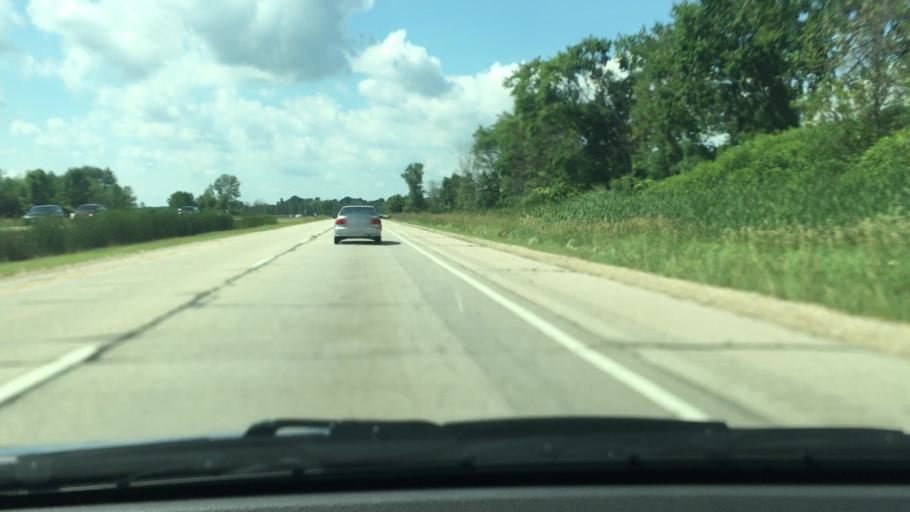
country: US
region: Wisconsin
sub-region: Dodge County
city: Theresa
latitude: 43.4529
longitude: -88.3601
